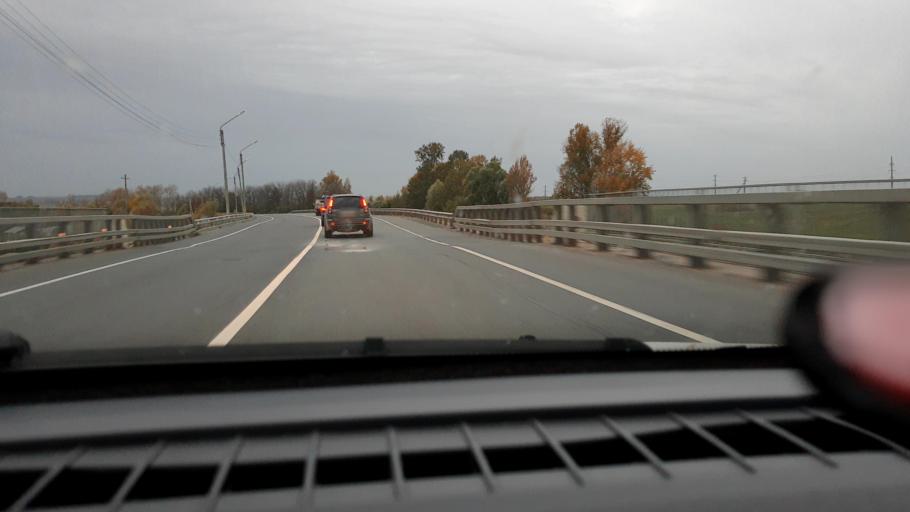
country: RU
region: Vladimir
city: Orgtrud
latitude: 56.2110
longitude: 40.5871
